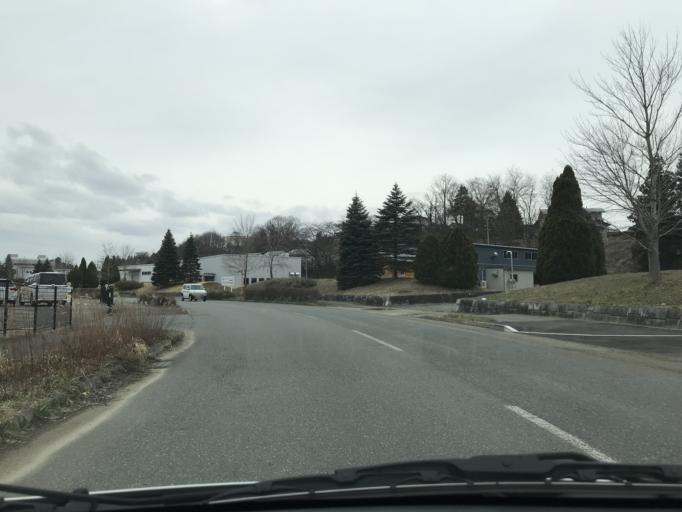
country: JP
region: Iwate
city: Kitakami
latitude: 39.2609
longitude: 141.1099
